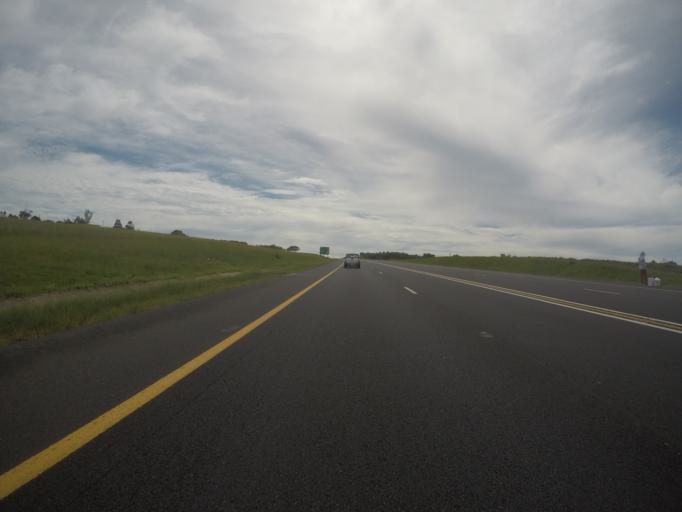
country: ZA
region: KwaZulu-Natal
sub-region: iLembe District Municipality
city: Mandeni
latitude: -29.0913
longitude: 31.6035
